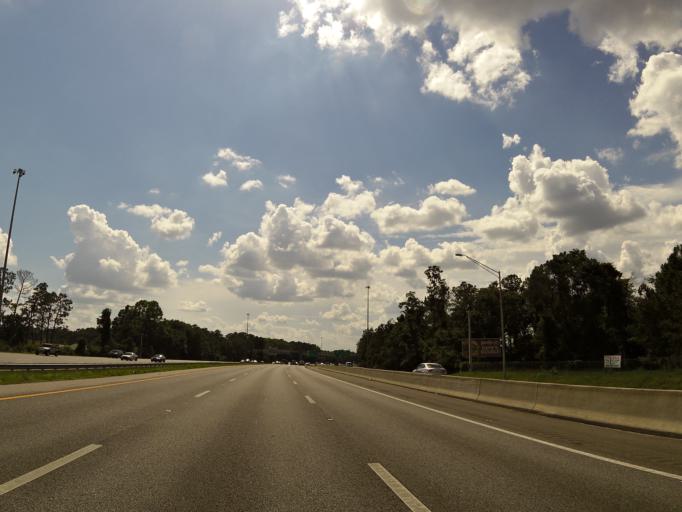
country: US
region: Florida
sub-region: Clay County
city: Bellair-Meadowbrook Terrace
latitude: 30.1914
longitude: -81.7210
